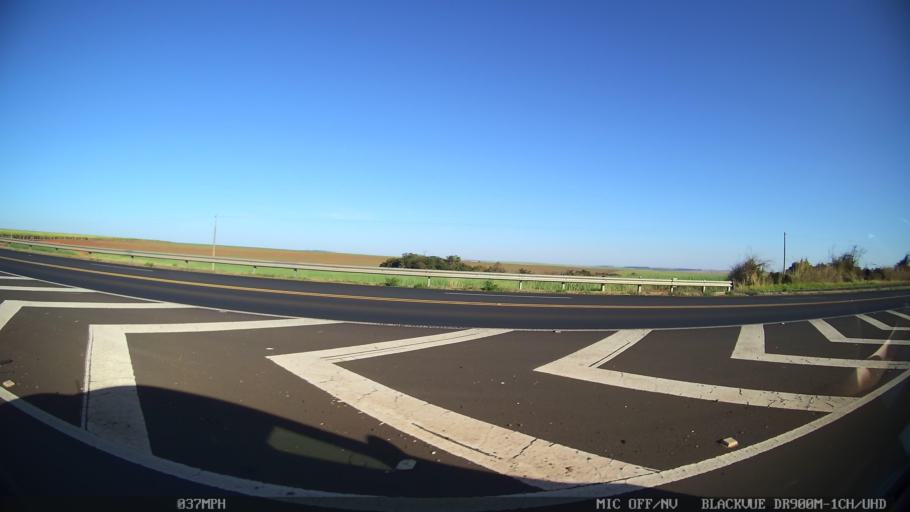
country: BR
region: Sao Paulo
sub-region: Guapiacu
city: Guapiacu
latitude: -20.7377
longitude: -49.0840
